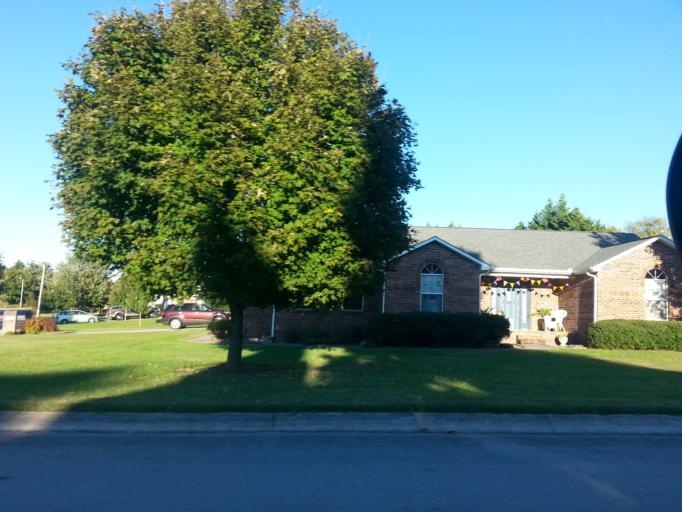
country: US
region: Tennessee
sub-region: Blount County
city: Eagleton Village
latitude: 35.7704
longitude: -83.9185
